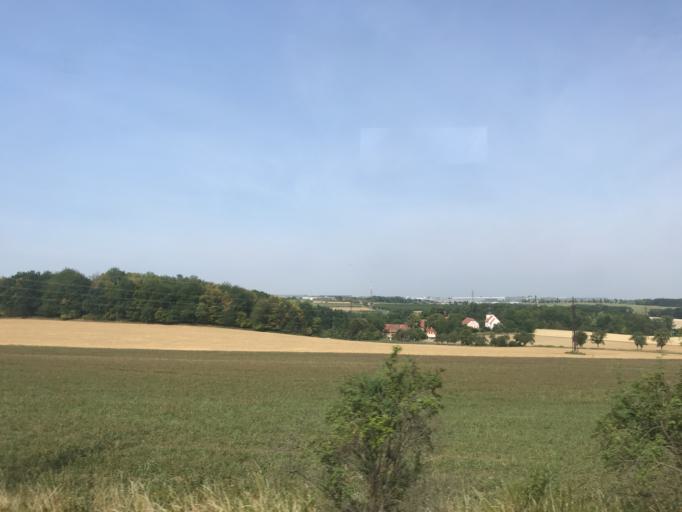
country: CZ
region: Central Bohemia
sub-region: Okres Praha-Vychod
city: Ricany
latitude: 49.9634
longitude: 14.6536
